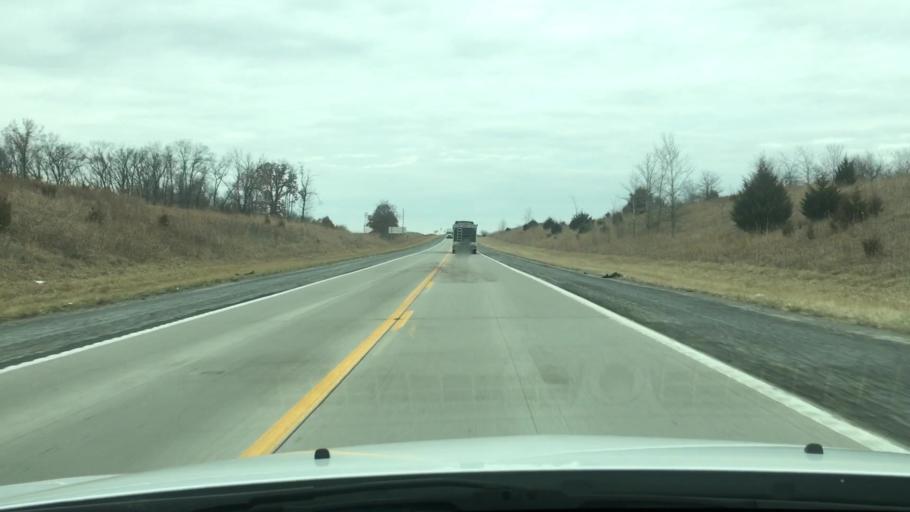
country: US
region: Missouri
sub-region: Audrain County
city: Mexico
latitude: 39.1494
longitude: -91.8437
